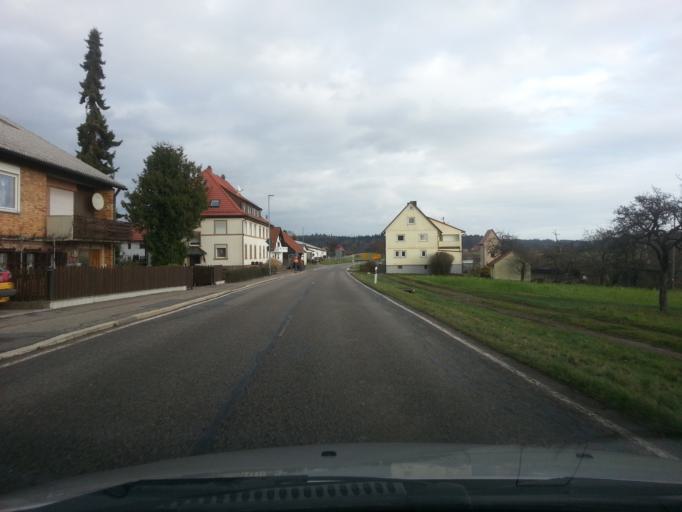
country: DE
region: Baden-Wuerttemberg
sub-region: Karlsruhe Region
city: Zwingenberg
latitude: 49.4624
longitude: 9.0810
